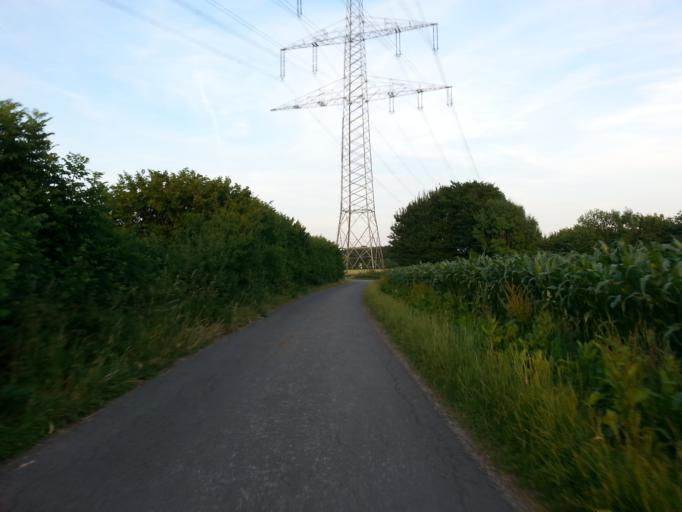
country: DE
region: North Rhine-Westphalia
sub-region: Regierungsbezirk Munster
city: Havixbeck
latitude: 51.9523
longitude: 7.4885
